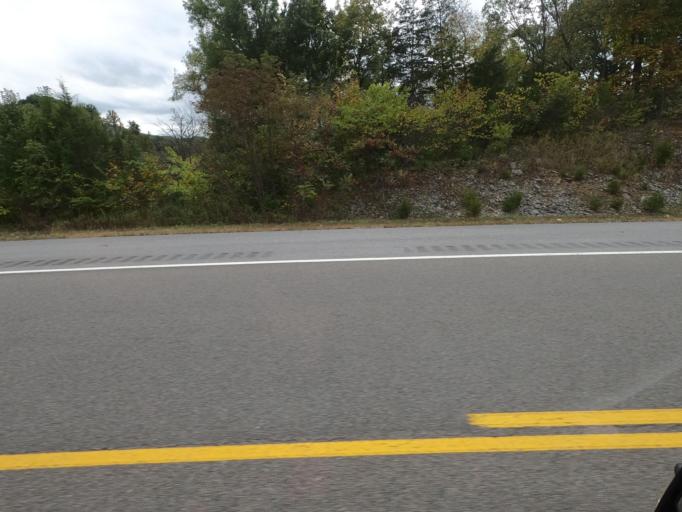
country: US
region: Tennessee
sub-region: Carter County
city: Central
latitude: 36.2851
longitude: -82.2446
